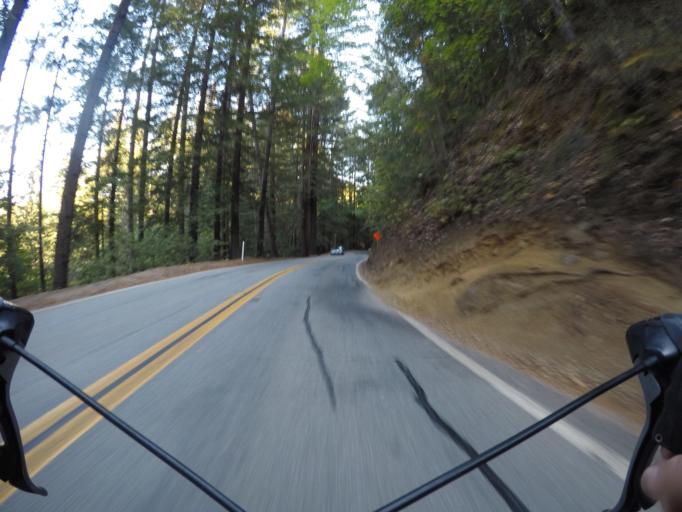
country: US
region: California
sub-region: Santa Cruz County
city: Pasatiempo
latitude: 37.0134
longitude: -122.0581
